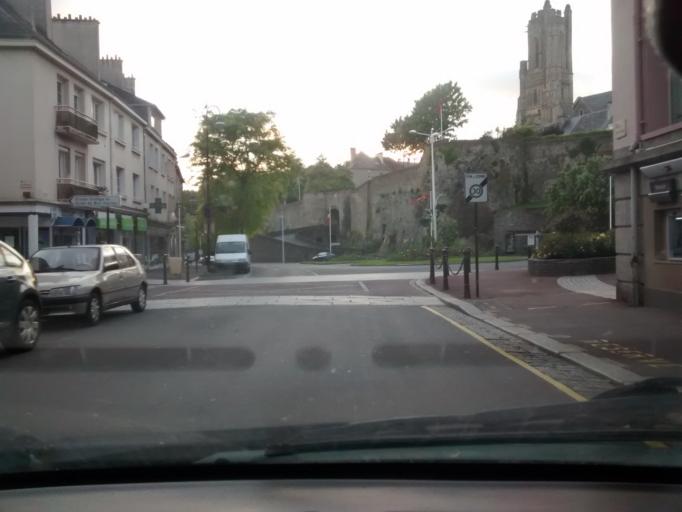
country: FR
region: Lower Normandy
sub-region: Departement de la Manche
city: Saint-Lo
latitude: 49.1143
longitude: -1.0931
